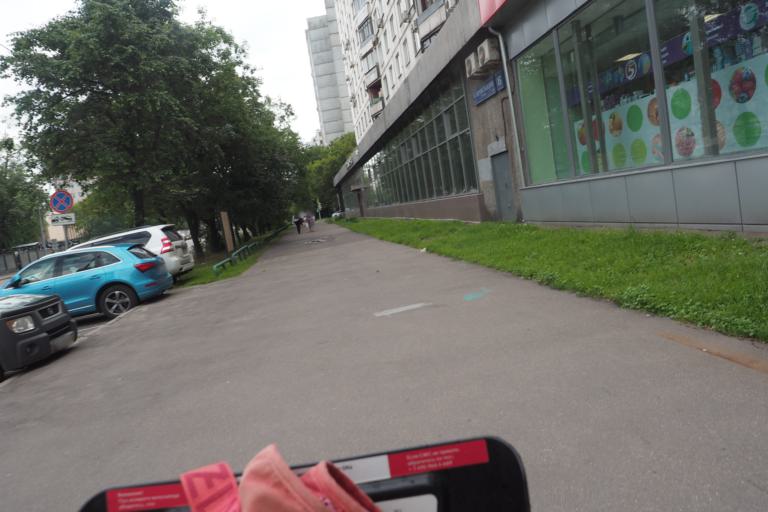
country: RU
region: Moscow
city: Mar'ina Roshcha
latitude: 55.7866
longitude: 37.6402
